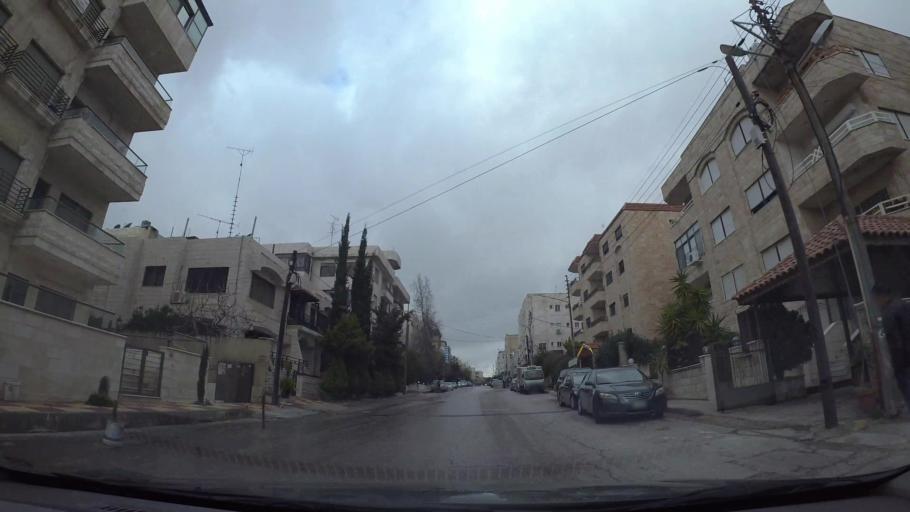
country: JO
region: Amman
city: Wadi as Sir
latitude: 31.9487
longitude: 35.8716
